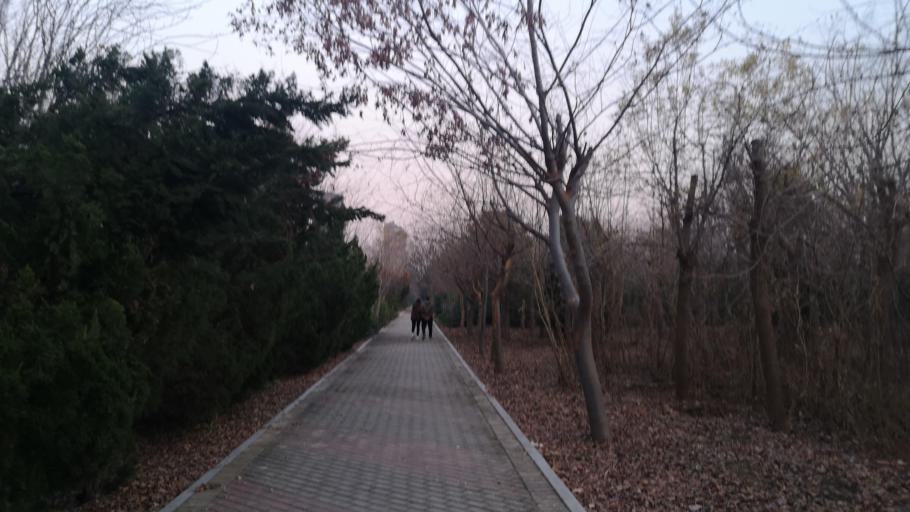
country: CN
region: Henan Sheng
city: Zhongyuanlu
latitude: 35.7423
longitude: 115.0608
